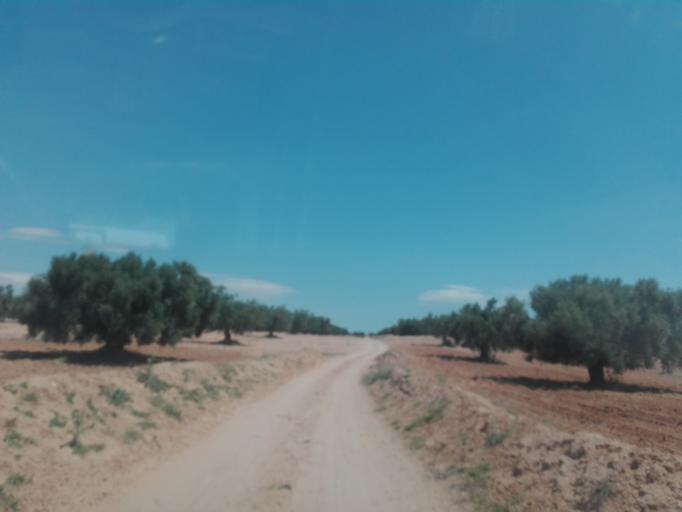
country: TN
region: Safaqis
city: Sfax
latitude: 34.6612
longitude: 10.6030
